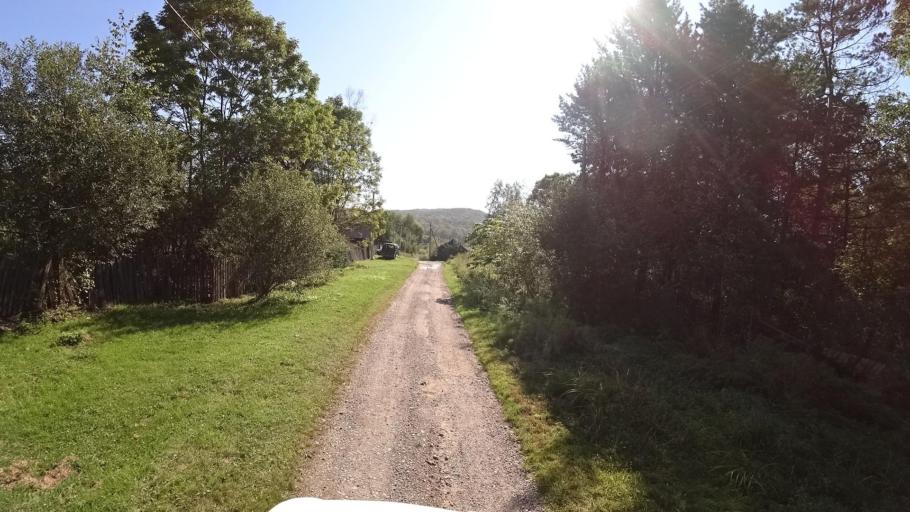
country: RU
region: Jewish Autonomous Oblast
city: Bira
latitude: 49.0021
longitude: 132.4739
